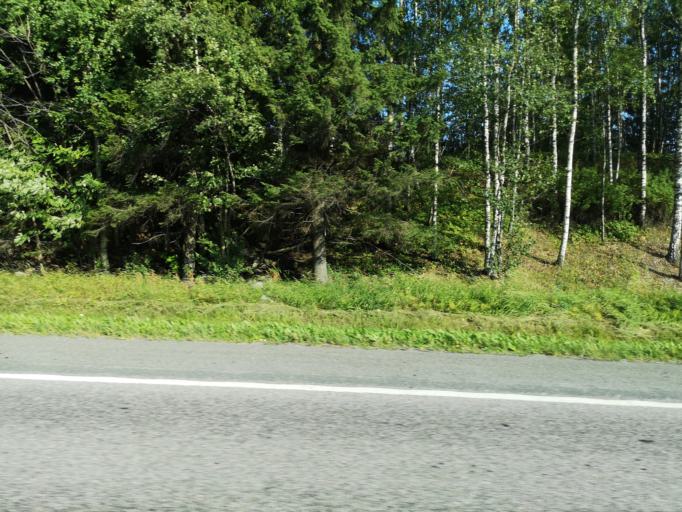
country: FI
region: Uusimaa
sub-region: Helsinki
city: Kerava
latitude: 60.3550
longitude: 25.1119
